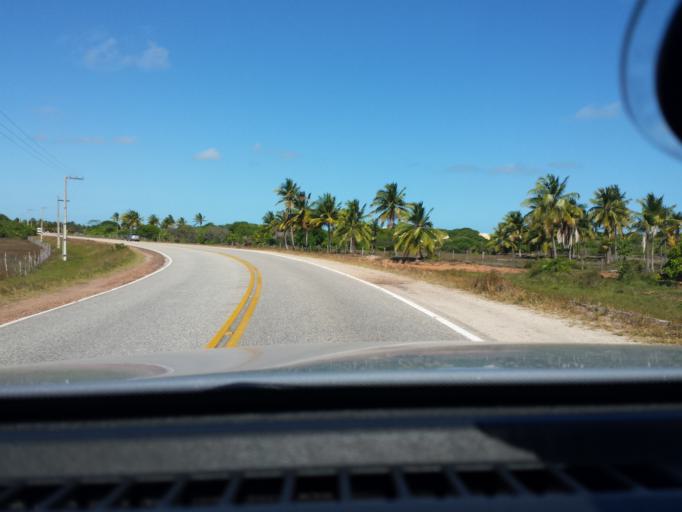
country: BR
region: Sergipe
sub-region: Estancia
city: Estancia
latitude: -11.2655
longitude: -37.2655
